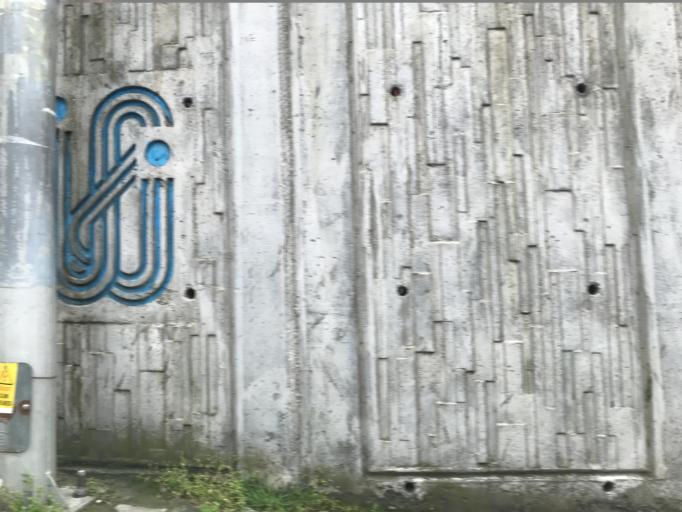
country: TR
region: Istanbul
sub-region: Atasehir
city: Atasehir
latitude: 40.9861
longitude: 29.0924
